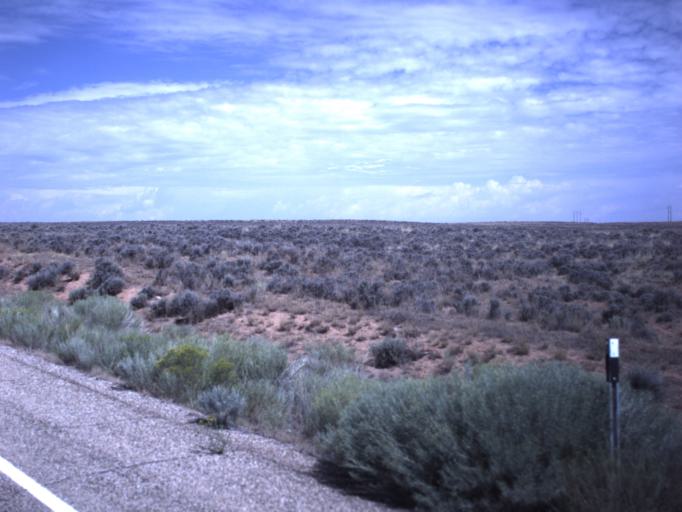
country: US
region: Utah
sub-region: Uintah County
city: Naples
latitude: 40.1479
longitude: -109.2935
